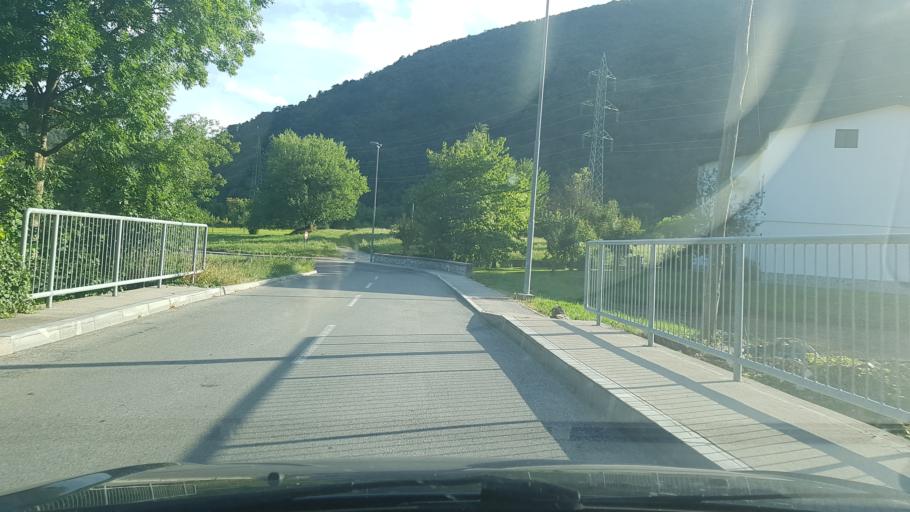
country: SI
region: Nova Gorica
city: Solkan
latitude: 46.0008
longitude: 13.6708
